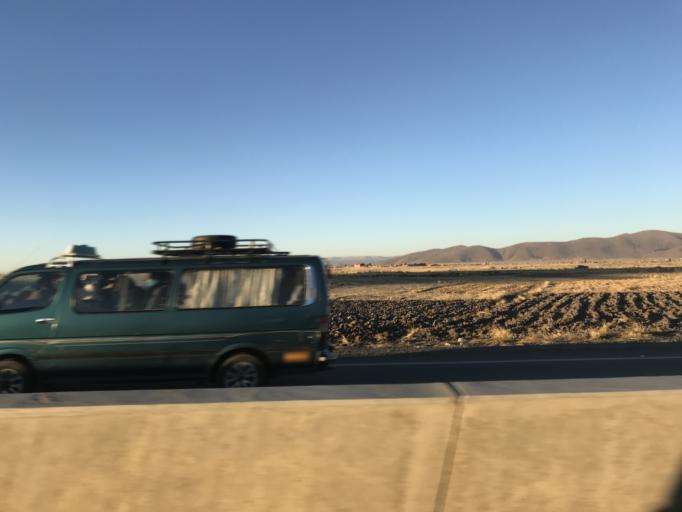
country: BO
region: La Paz
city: Batallas
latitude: -16.2986
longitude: -68.5211
